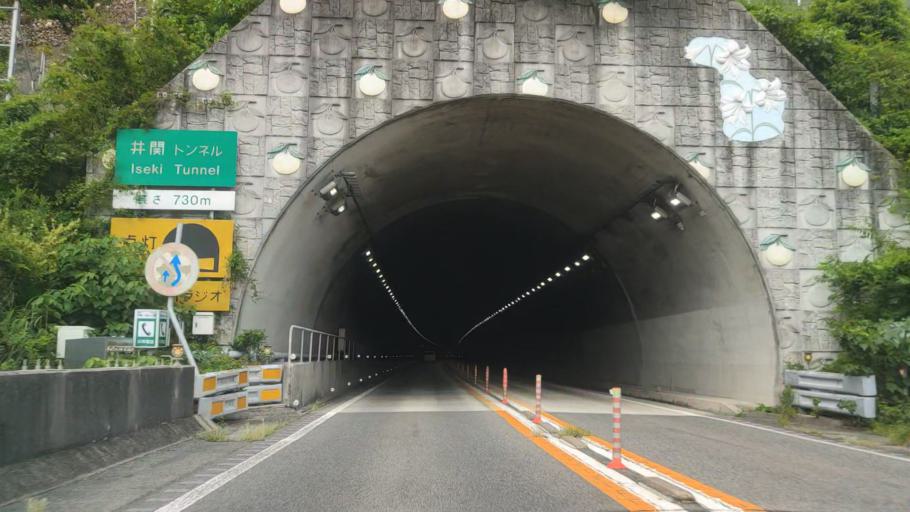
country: JP
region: Wakayama
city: Gobo
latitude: 33.9991
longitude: 135.1959
